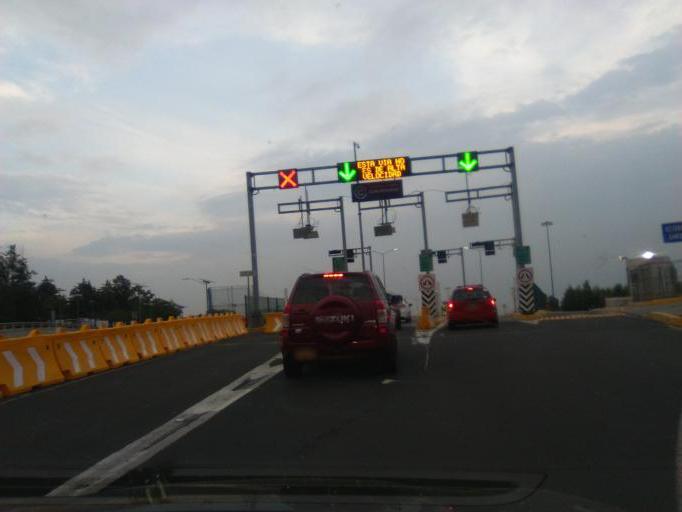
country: MX
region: Mexico City
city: Col. Bosques de las Lomas
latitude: 19.3464
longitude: -99.2535
